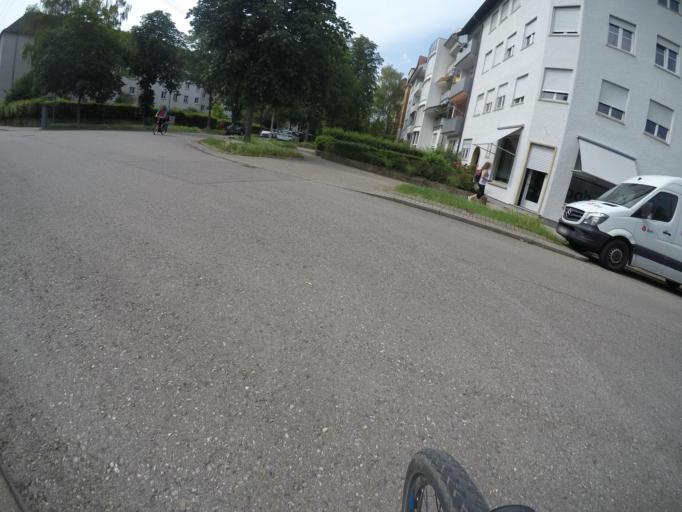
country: DE
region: Baden-Wuerttemberg
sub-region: Regierungsbezirk Stuttgart
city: Stuttgart-Ost
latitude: 48.8019
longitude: 9.2302
